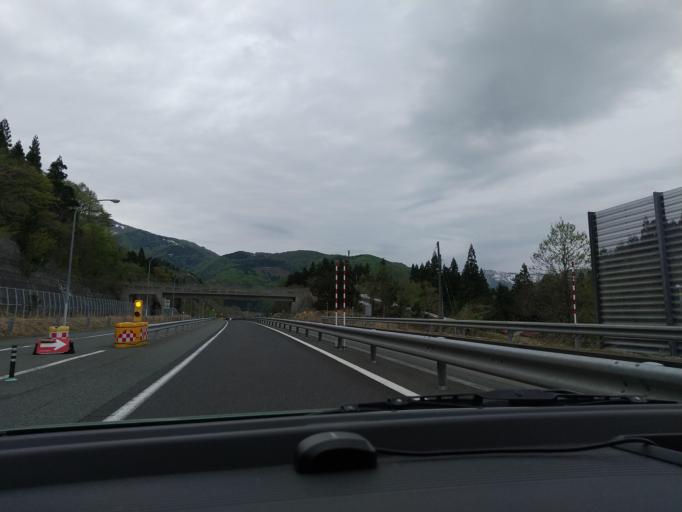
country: JP
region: Iwate
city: Kitakami
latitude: 39.2976
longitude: 140.9352
